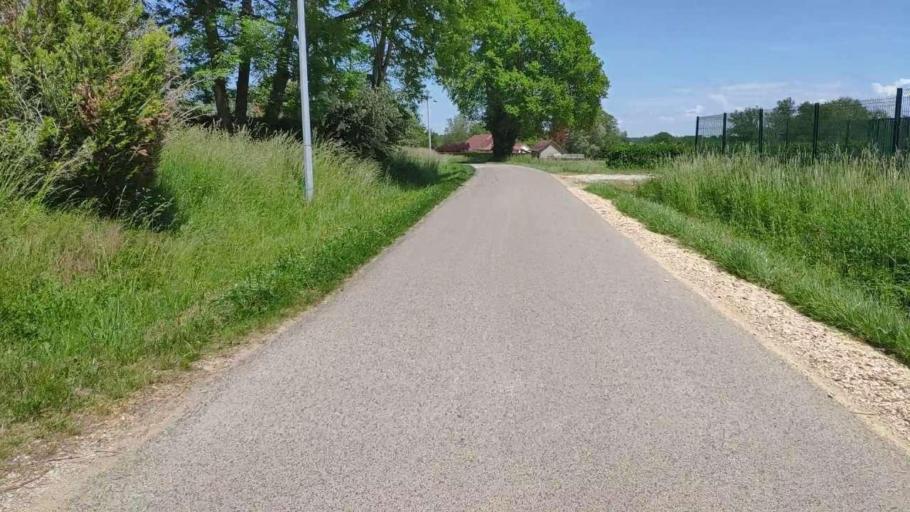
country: FR
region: Franche-Comte
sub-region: Departement du Jura
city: Bletterans
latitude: 46.7908
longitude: 5.3752
